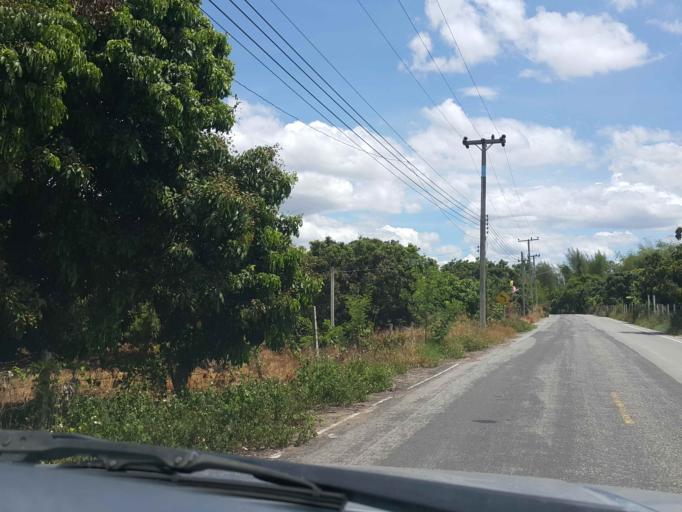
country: TH
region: Chiang Mai
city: Doi Lo
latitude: 18.5271
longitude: 98.7761
